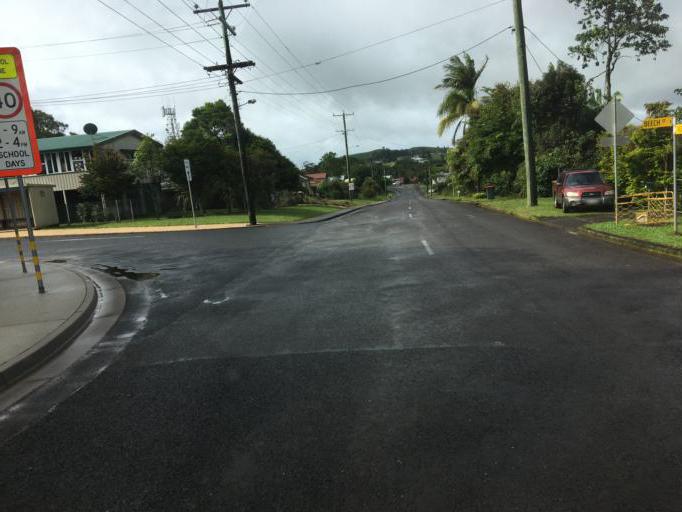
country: AU
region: Queensland
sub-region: Tablelands
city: Ravenshoe
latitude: -17.5132
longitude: 145.6102
